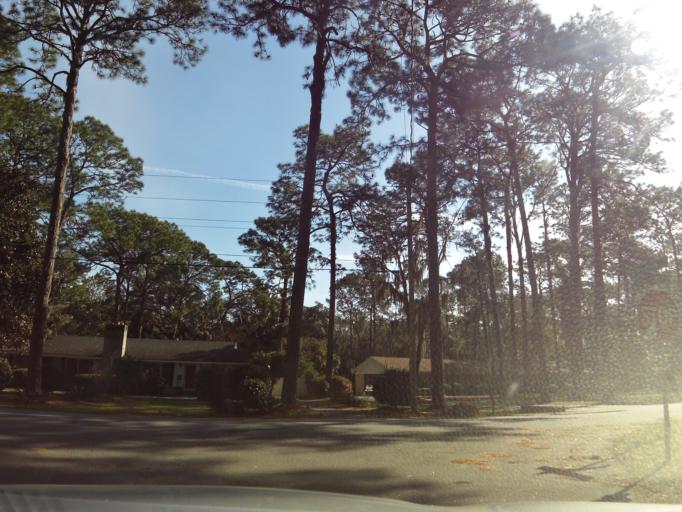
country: US
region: Georgia
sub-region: Lowndes County
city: Remerton
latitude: 30.8538
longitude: -83.3045
